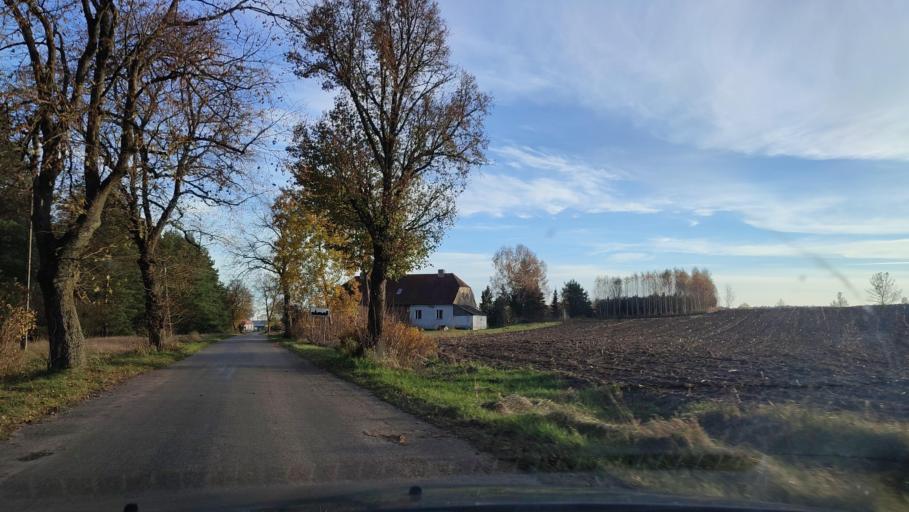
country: PL
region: Masovian Voivodeship
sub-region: Powiat przasnyski
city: Chorzele
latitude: 53.3434
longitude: 20.7520
